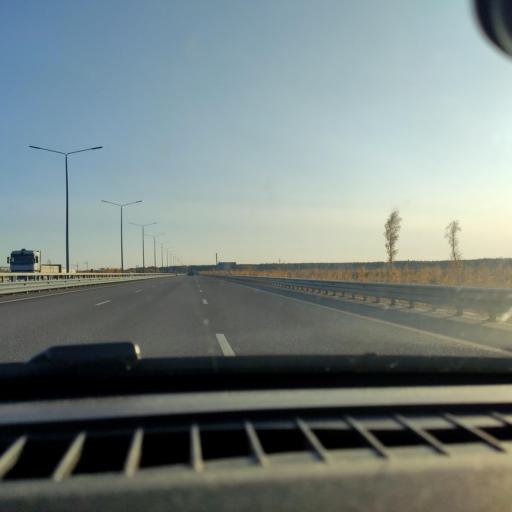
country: RU
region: Voronezj
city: Somovo
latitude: 51.7572
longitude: 39.3068
